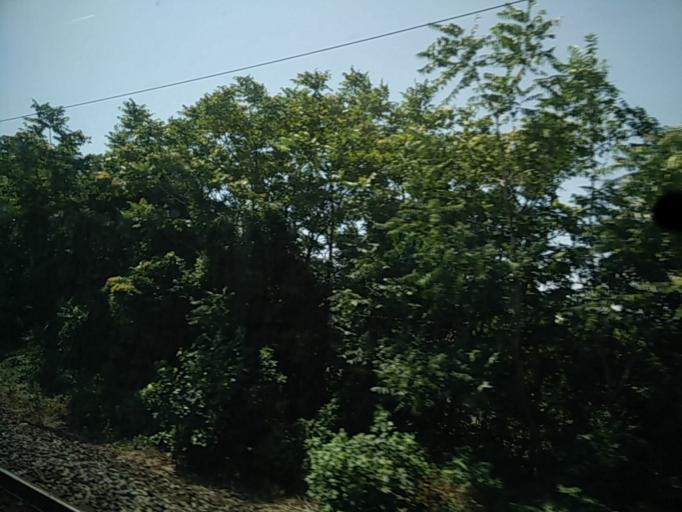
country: FR
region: Ile-de-France
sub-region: Departement du Val-de-Marne
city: Champigny-sur-Marne
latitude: 48.8268
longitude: 2.5022
